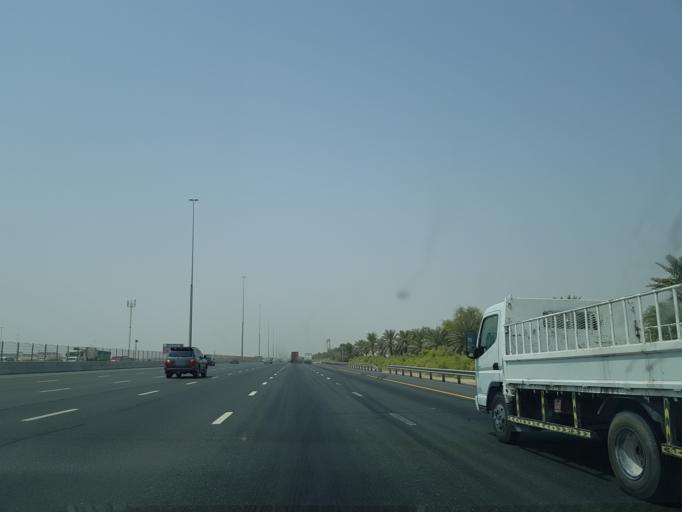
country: AE
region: Dubai
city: Dubai
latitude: 25.0748
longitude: 55.3053
